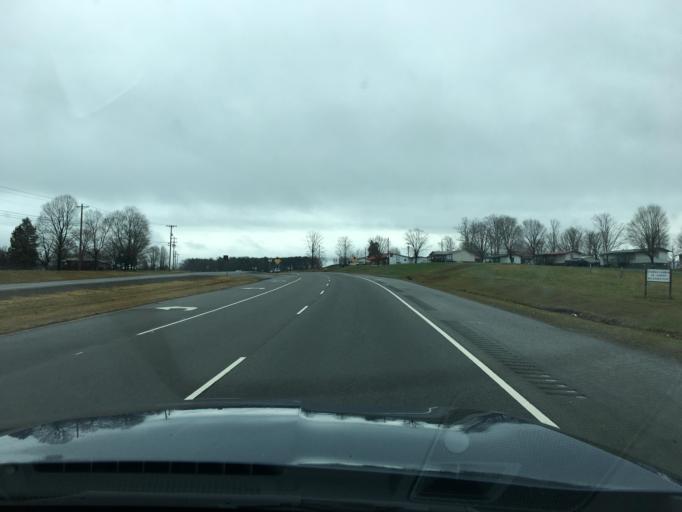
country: US
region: Tennessee
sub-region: McMinn County
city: Etowah
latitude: 35.3423
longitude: -84.5414
